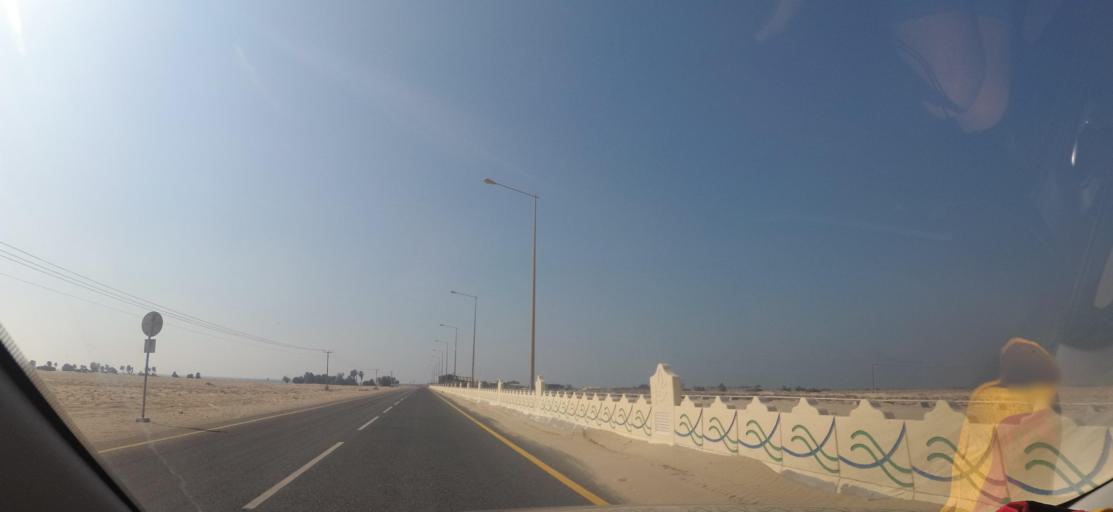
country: QA
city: Umm Bab
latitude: 25.2107
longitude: 50.7728
